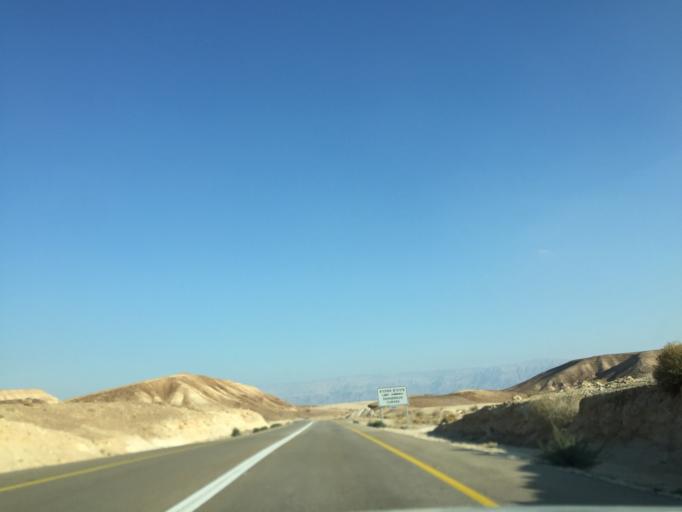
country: IL
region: Southern District
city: `En Boqeq
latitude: 31.1750
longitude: 35.3009
